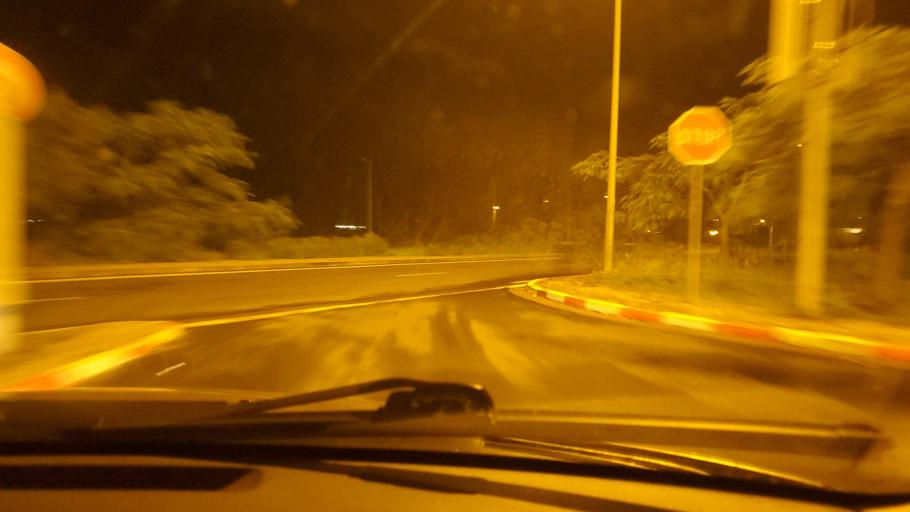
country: SN
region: Thies
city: Pout
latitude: 14.6684
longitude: -17.0659
